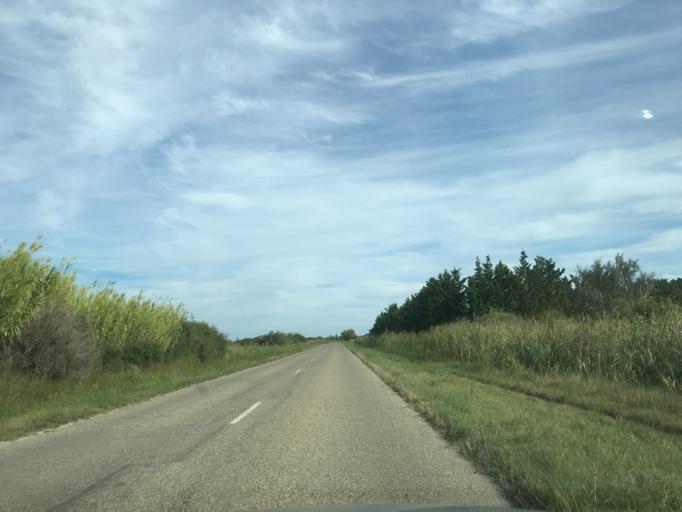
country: FR
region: Provence-Alpes-Cote d'Azur
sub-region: Departement des Bouches-du-Rhone
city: Saintes-Maries-de-la-Mer
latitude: 43.5241
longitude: 4.3811
